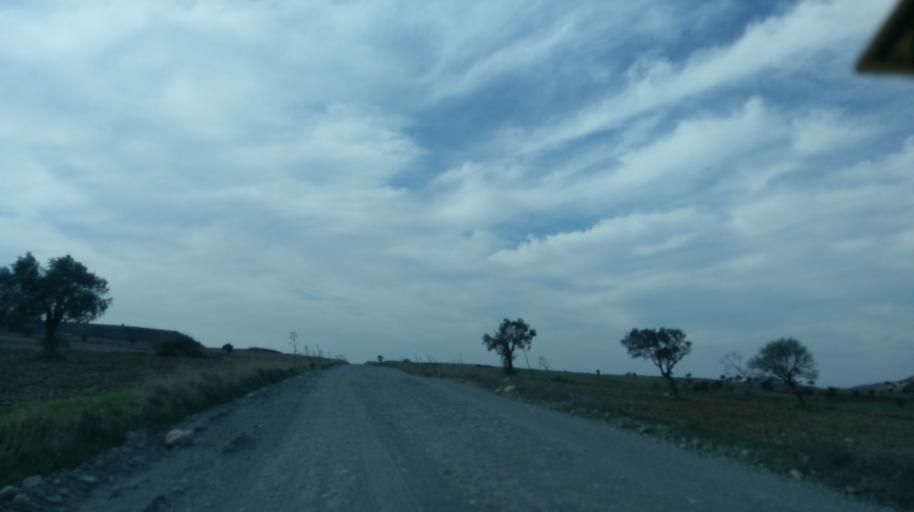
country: CY
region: Keryneia
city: Lapithos
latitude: 35.2844
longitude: 33.1571
